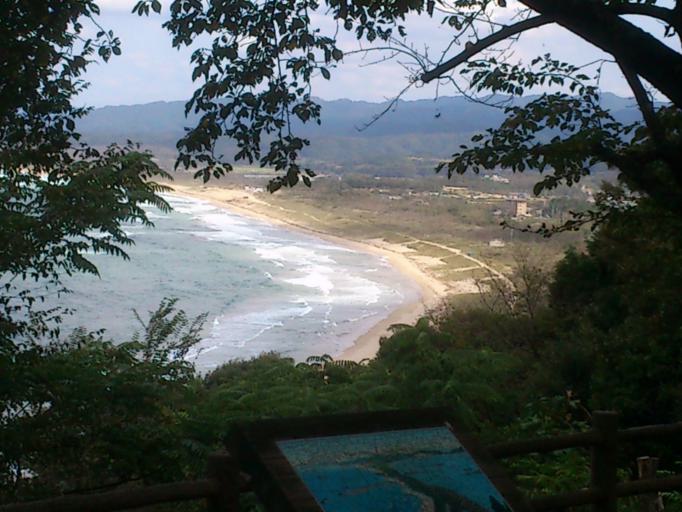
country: JP
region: Hyogo
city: Toyooka
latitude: 35.6457
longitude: 134.9009
